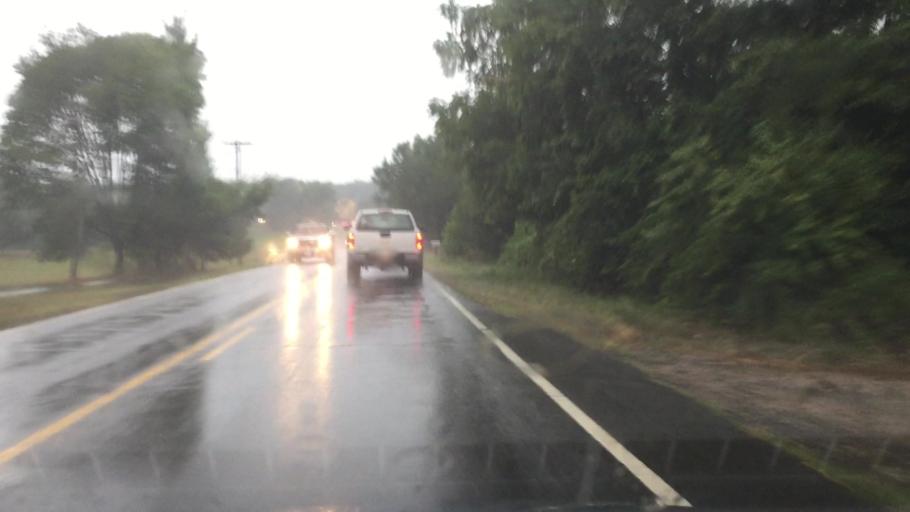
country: US
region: North Carolina
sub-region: Gaston County
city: Davidson
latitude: 35.5230
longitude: -80.7702
